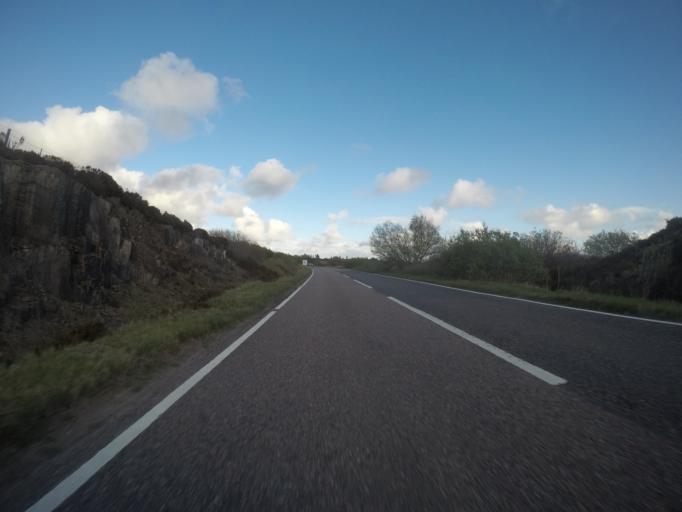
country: GB
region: Scotland
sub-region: Highland
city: Portree
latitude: 57.4587
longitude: -6.2768
